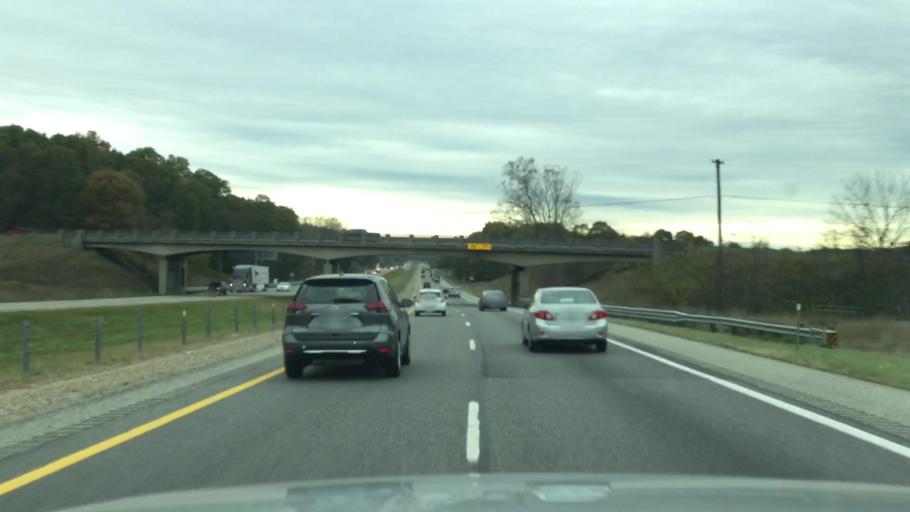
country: US
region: Michigan
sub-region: Van Buren County
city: Mattawan
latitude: 42.2363
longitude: -85.7052
